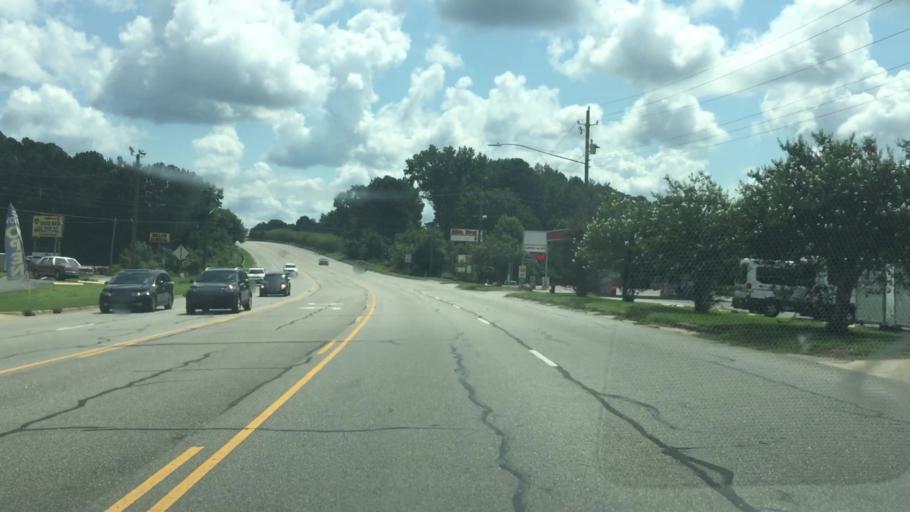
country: US
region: North Carolina
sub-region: Anson County
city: Wadesboro
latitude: 34.9632
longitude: -80.0547
